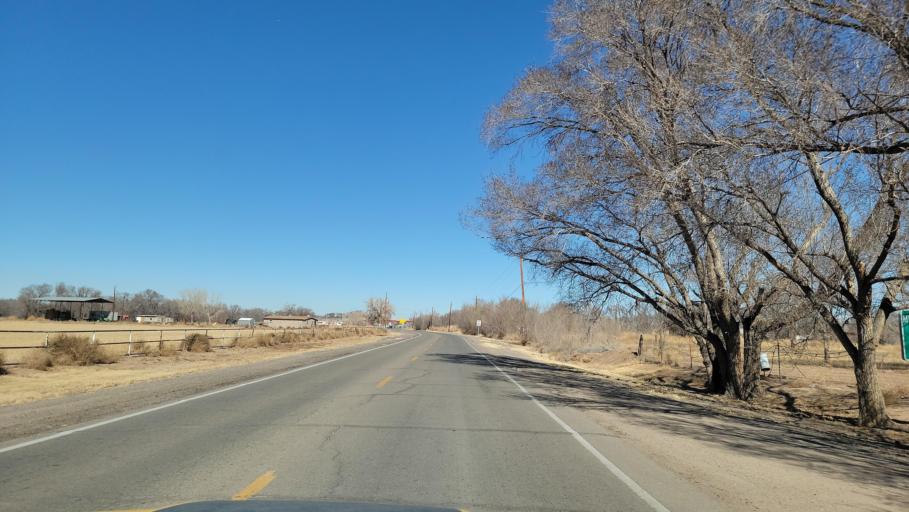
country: US
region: New Mexico
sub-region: Bernalillo County
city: South Valley
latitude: 34.9428
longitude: -106.6923
